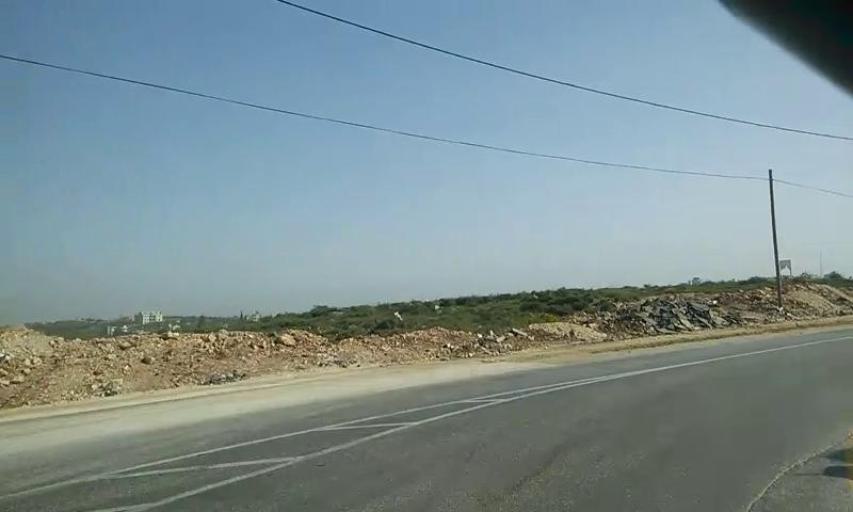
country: PS
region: West Bank
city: Surda
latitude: 31.9364
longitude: 35.2076
